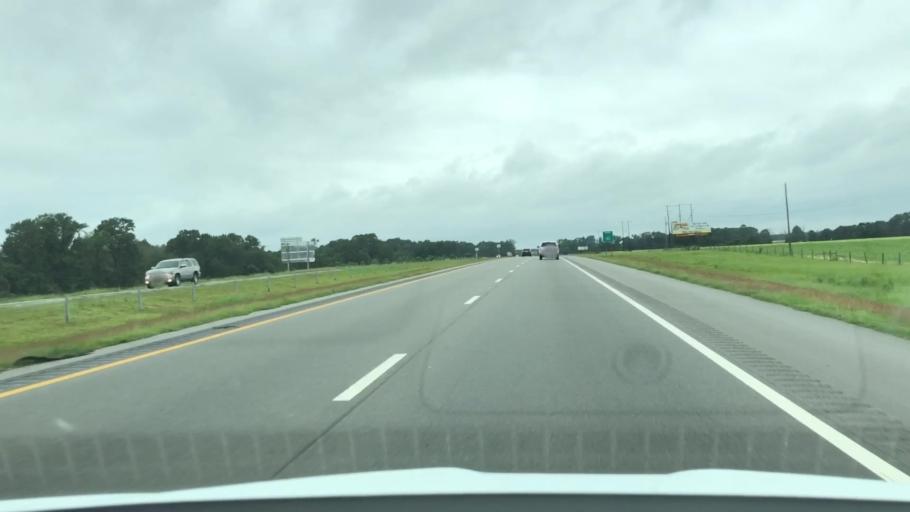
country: US
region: North Carolina
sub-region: Lenoir County
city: La Grange
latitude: 35.3132
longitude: -77.8268
